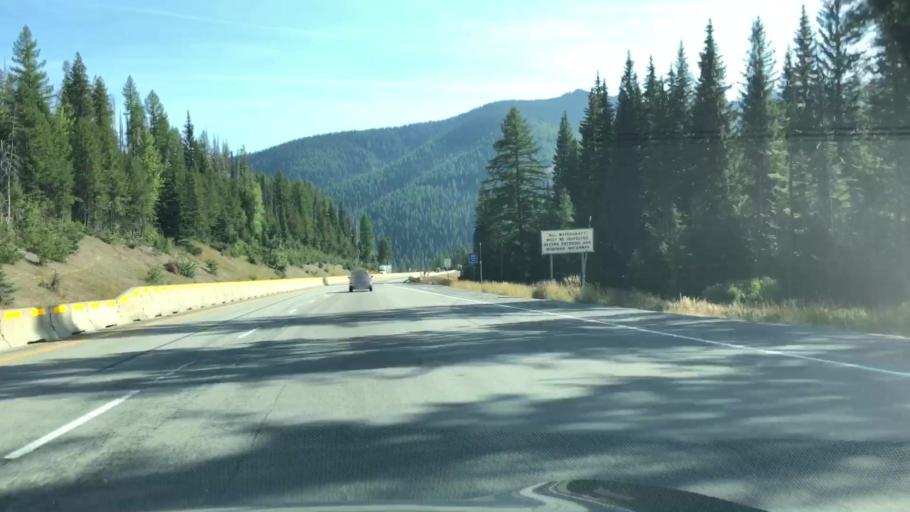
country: US
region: Idaho
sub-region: Shoshone County
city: Wallace
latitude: 47.4530
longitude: -115.6943
